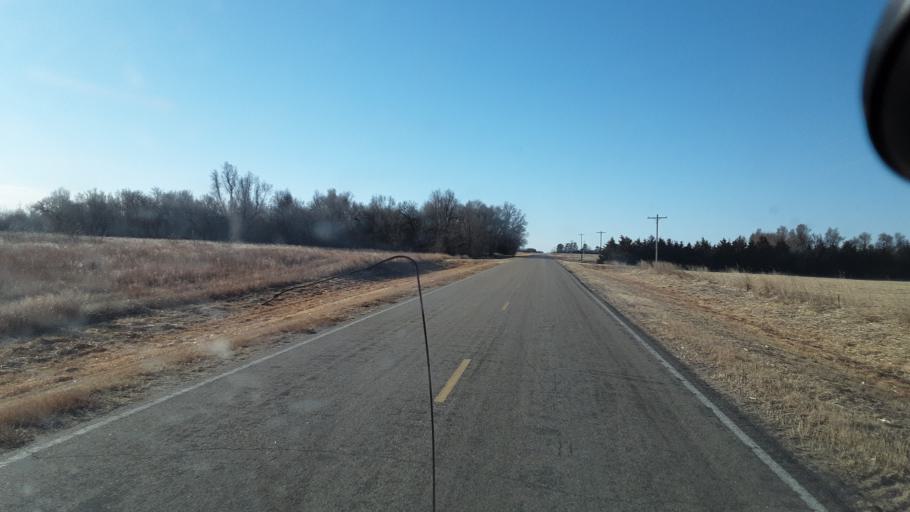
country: US
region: Kansas
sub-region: Barton County
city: Ellinwood
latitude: 38.3281
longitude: -98.6653
